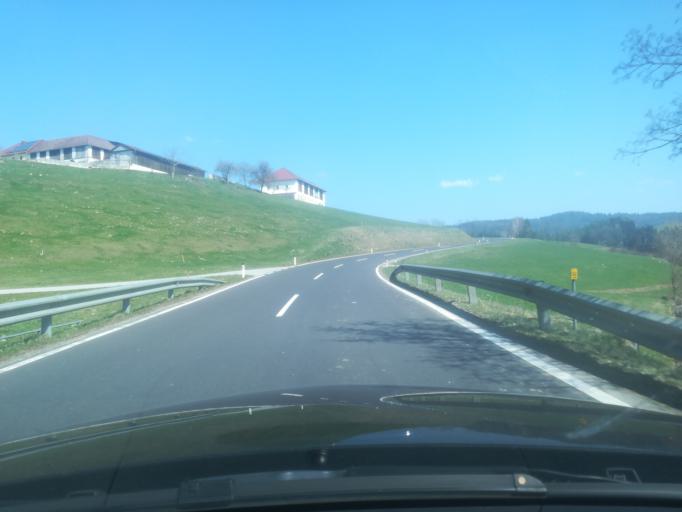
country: AT
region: Upper Austria
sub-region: Politischer Bezirk Perg
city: Perg
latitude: 48.3546
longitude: 14.6758
